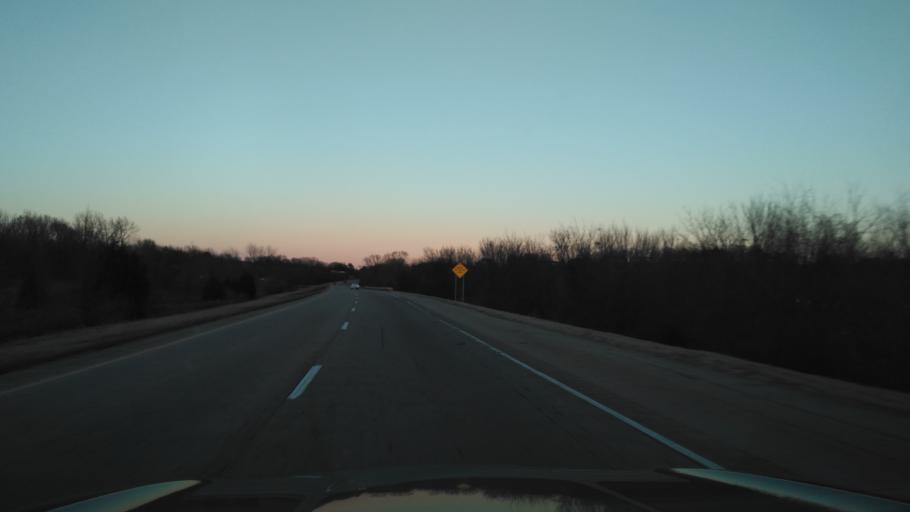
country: US
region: Arkansas
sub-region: Crawford County
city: Van Buren
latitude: 35.4614
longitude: -94.3874
